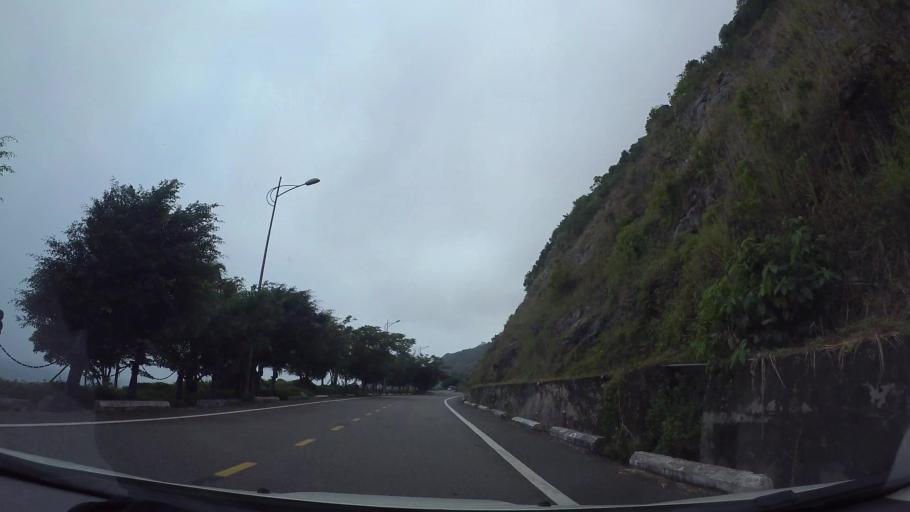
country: VN
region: Da Nang
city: Son Tra
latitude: 16.1086
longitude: 108.3083
